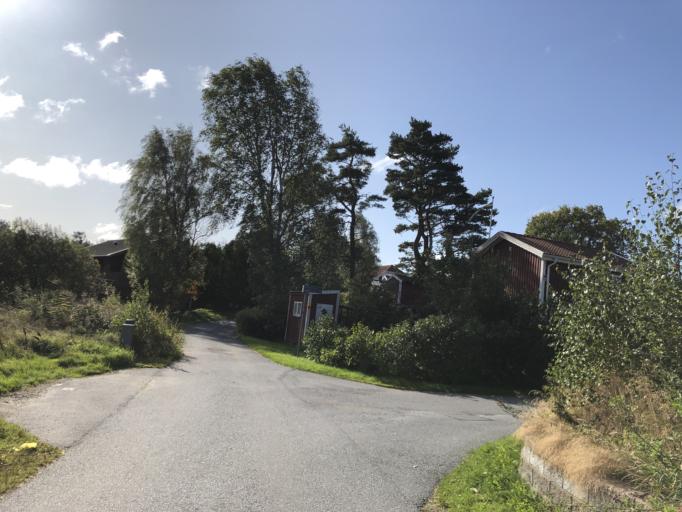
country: SE
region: Vaestra Goetaland
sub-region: Goteborg
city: Torslanda
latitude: 57.7350
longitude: 11.8170
